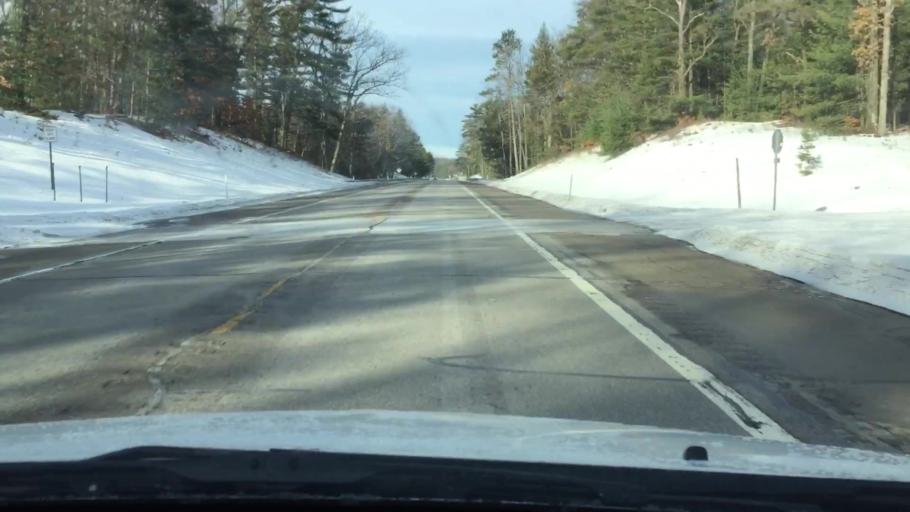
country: US
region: Michigan
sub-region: Wexford County
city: Manton
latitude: 44.5692
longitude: -85.3656
